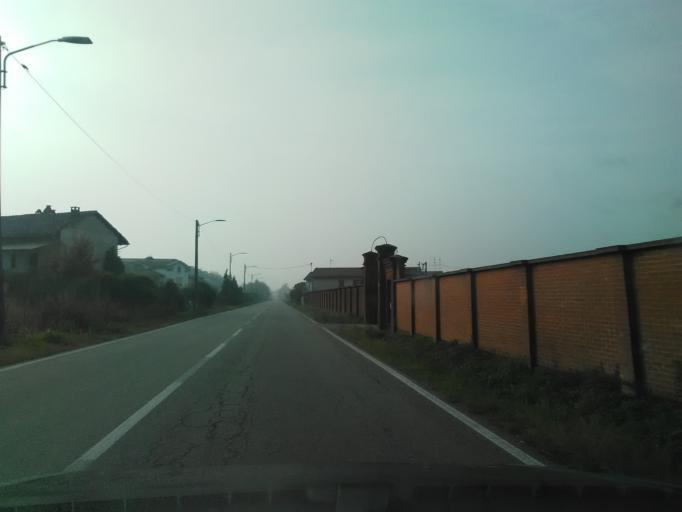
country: IT
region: Piedmont
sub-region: Provincia di Vercelli
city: Santhia
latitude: 45.3608
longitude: 8.1718
